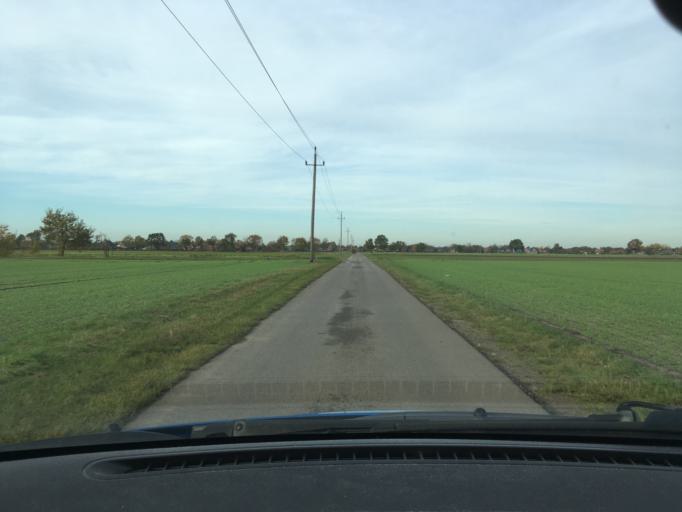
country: DE
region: Lower Saxony
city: Wittorf
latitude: 53.3201
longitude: 10.3726
